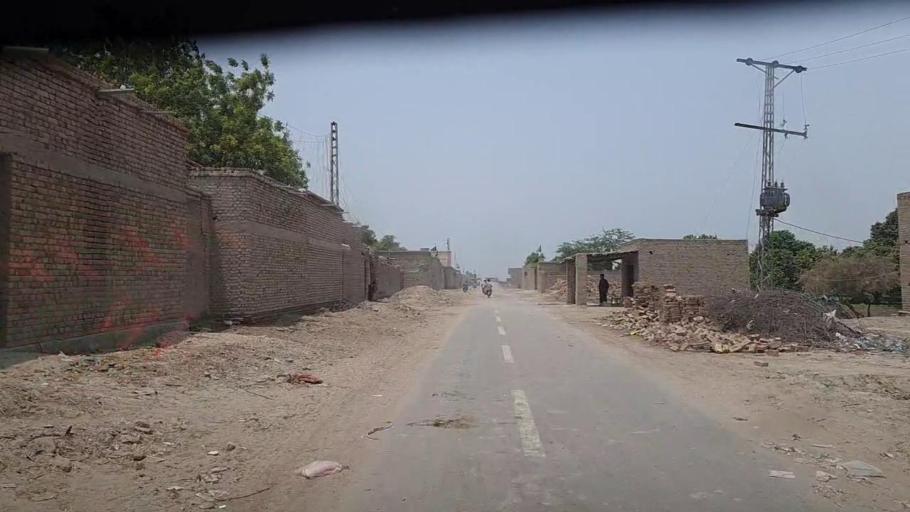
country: PK
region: Sindh
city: Sita Road
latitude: 27.0395
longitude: 67.8993
